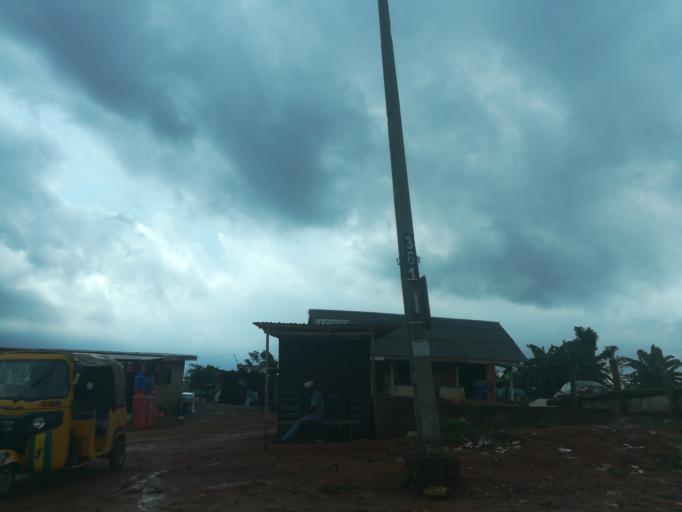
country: NG
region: Lagos
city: Ikorodu
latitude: 6.6618
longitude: 3.5929
